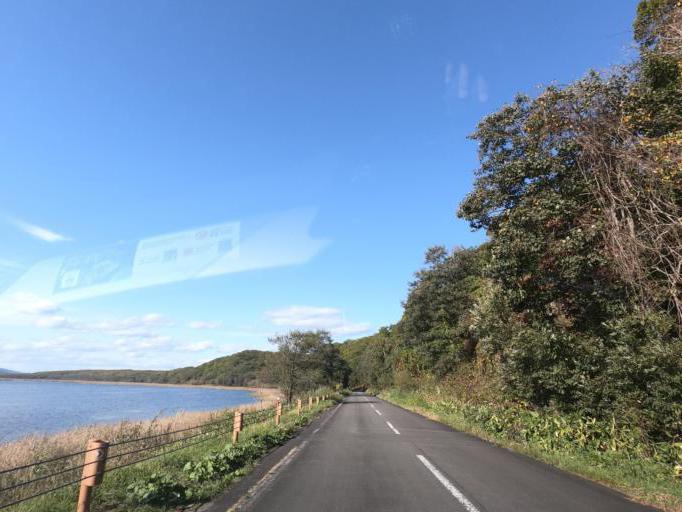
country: JP
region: Hokkaido
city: Obihiro
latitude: 42.6127
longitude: 143.5444
